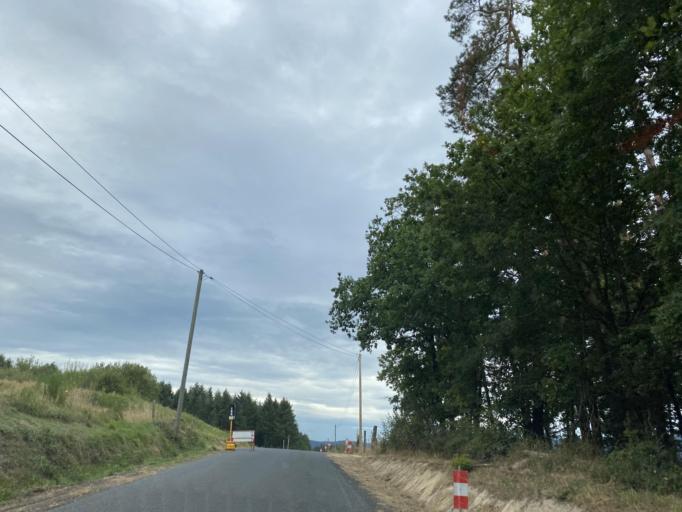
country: FR
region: Auvergne
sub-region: Departement du Puy-de-Dome
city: Marsac-en-Livradois
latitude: 45.5102
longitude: 3.7439
